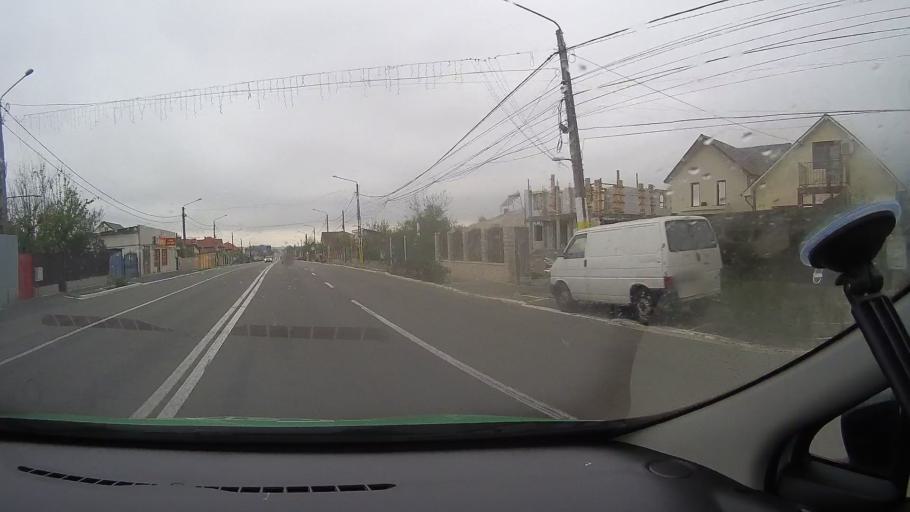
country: RO
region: Constanta
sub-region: Comuna Valu lui Traian
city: Valu lui Traian
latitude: 44.1648
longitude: 28.4716
